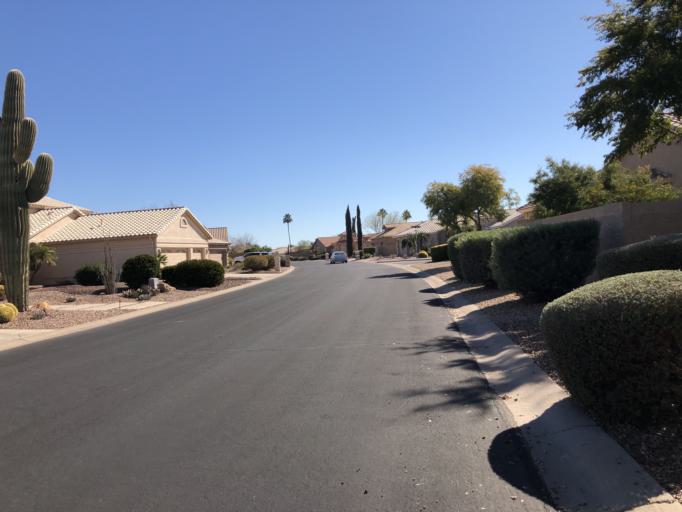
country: US
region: Arizona
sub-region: Maricopa County
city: Sun Lakes
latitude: 33.2273
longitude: -111.8854
